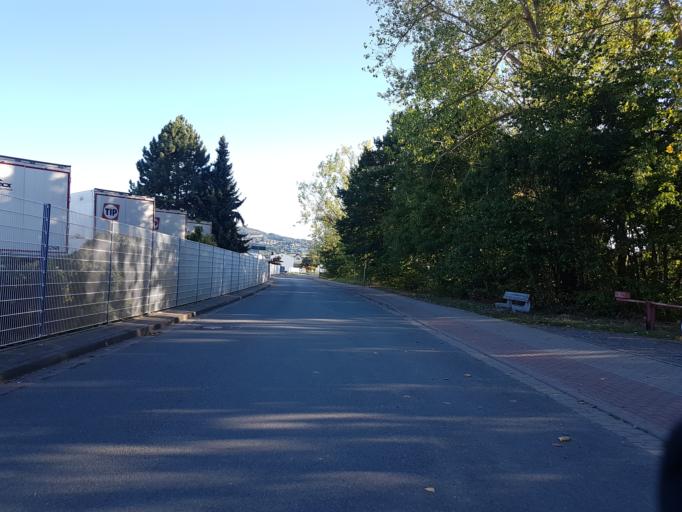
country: DE
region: North Rhine-Westphalia
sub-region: Regierungsbezirk Detmold
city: Vlotho
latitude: 52.1802
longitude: 8.8668
